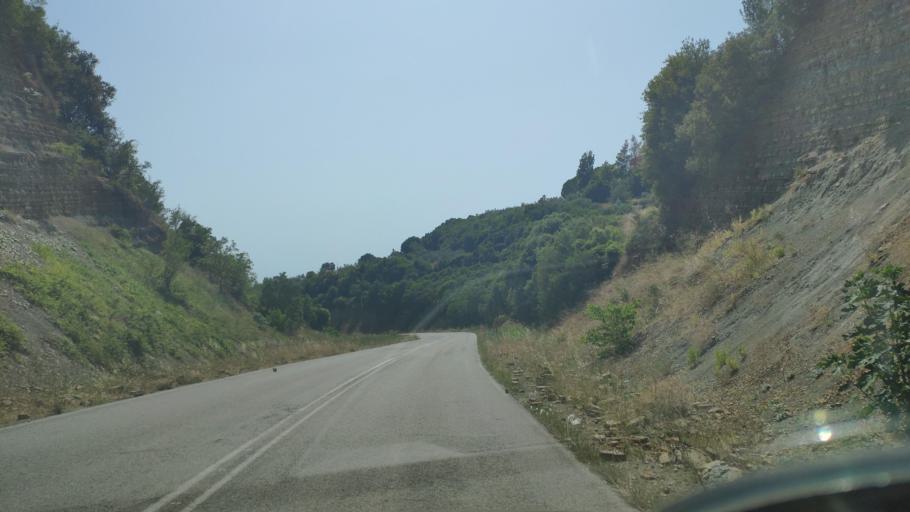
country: GR
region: Epirus
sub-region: Nomos Artas
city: Peta
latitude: 39.1775
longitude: 21.0815
